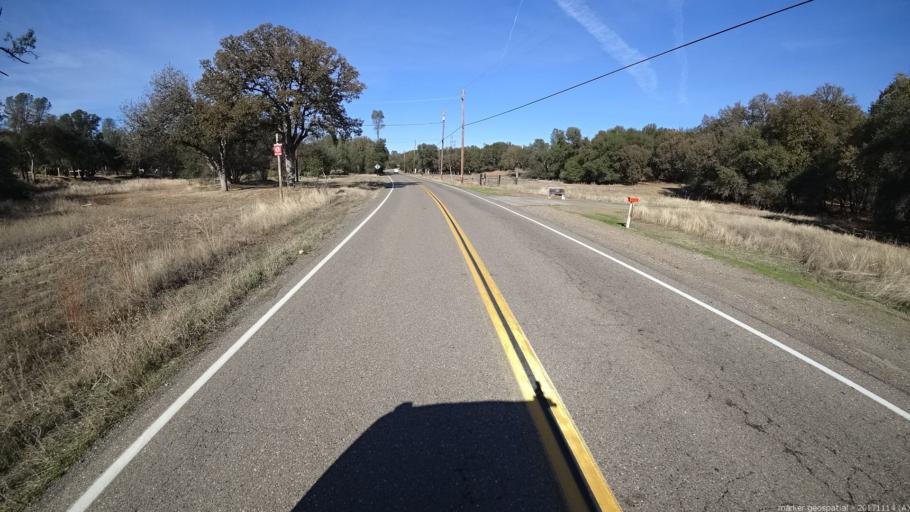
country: US
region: California
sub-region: Shasta County
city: Anderson
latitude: 40.3999
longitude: -122.3528
